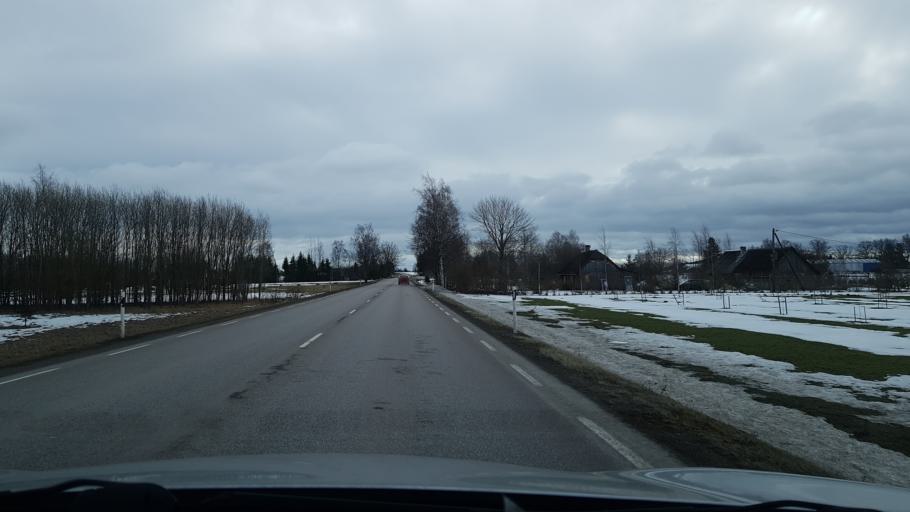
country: EE
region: Jogevamaa
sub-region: Jogeva linn
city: Jogeva
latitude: 58.6773
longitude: 26.4866
